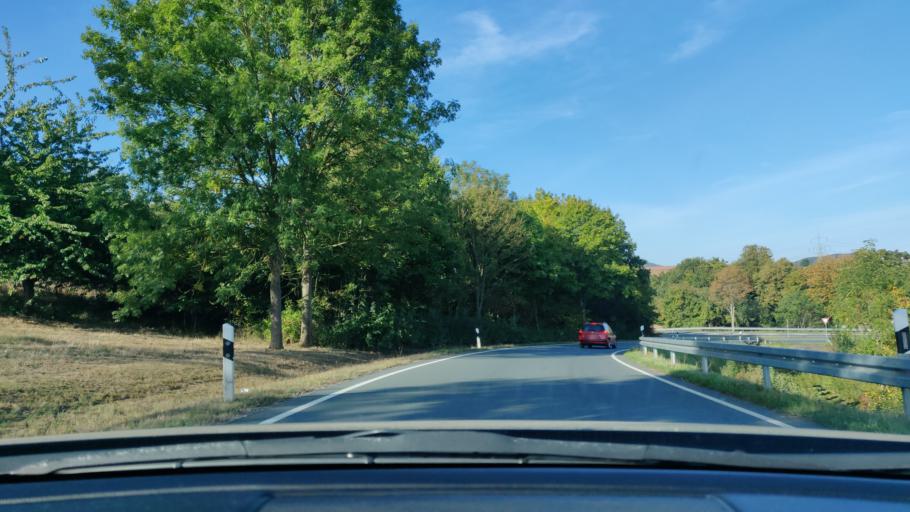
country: DE
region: Hesse
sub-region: Regierungsbezirk Kassel
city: Bad Wildungen
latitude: 51.1250
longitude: 9.1595
